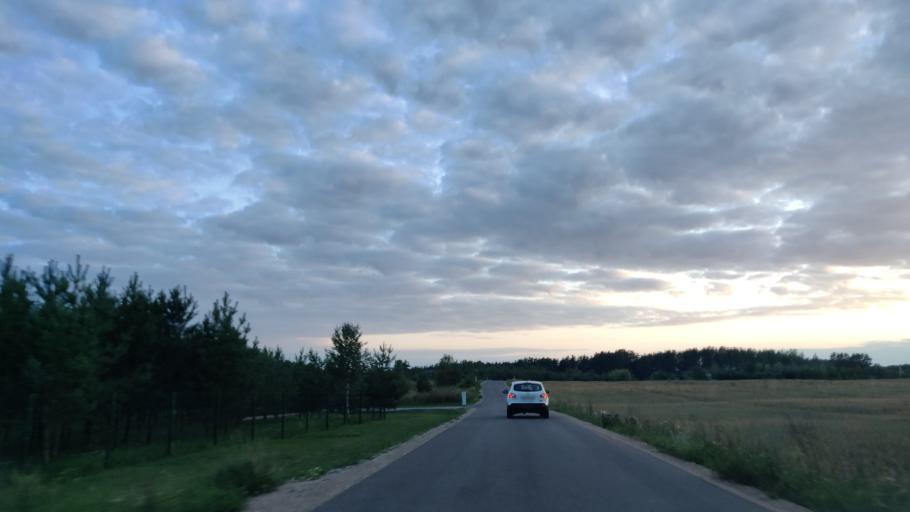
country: LT
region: Vilnius County
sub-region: Trakai
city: Rudiskes
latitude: 54.6056
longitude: 24.7918
